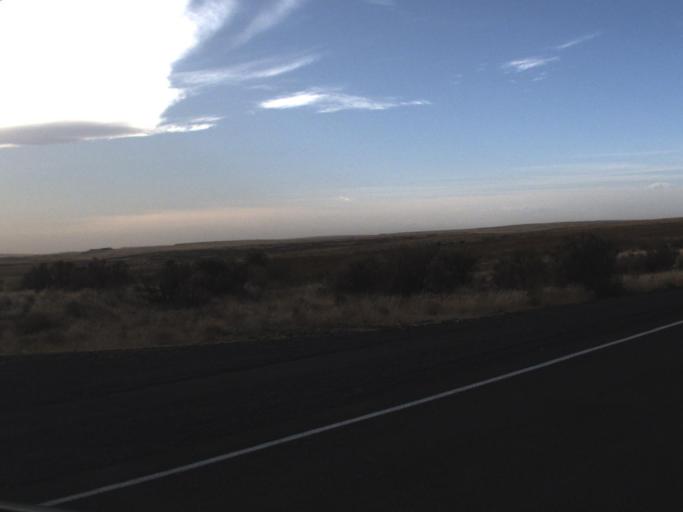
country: US
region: Washington
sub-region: Grant County
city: Warden
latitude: 47.3433
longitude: -118.9157
